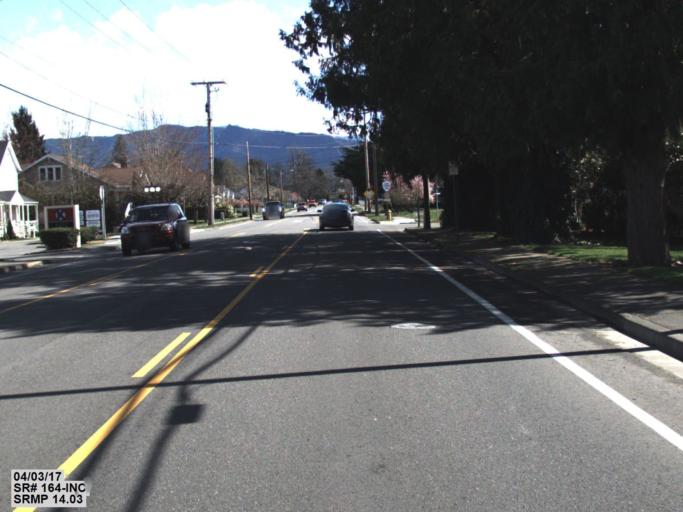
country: US
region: Washington
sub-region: King County
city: Enumclaw
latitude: 47.2066
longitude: -122.0007
